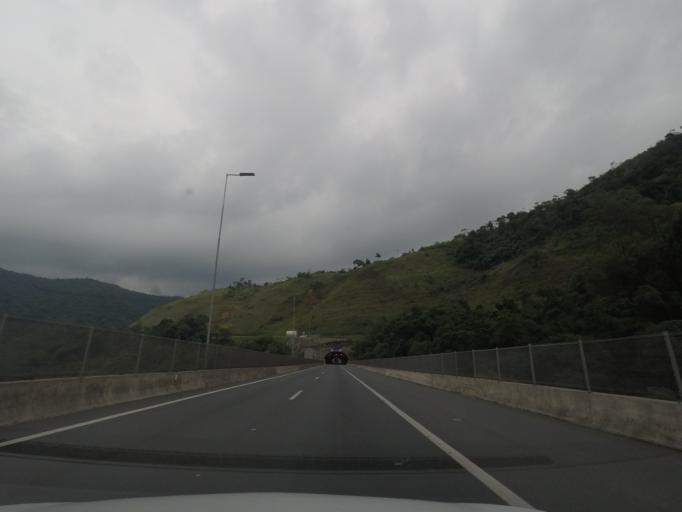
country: BR
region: Sao Paulo
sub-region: Miracatu
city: Miracatu
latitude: -24.1147
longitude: -47.2688
